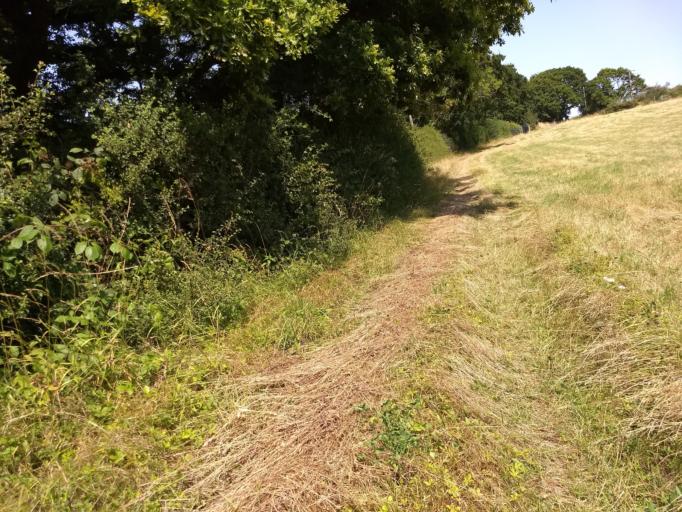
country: GB
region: England
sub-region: Isle of Wight
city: Northwood
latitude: 50.7295
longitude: -1.3370
